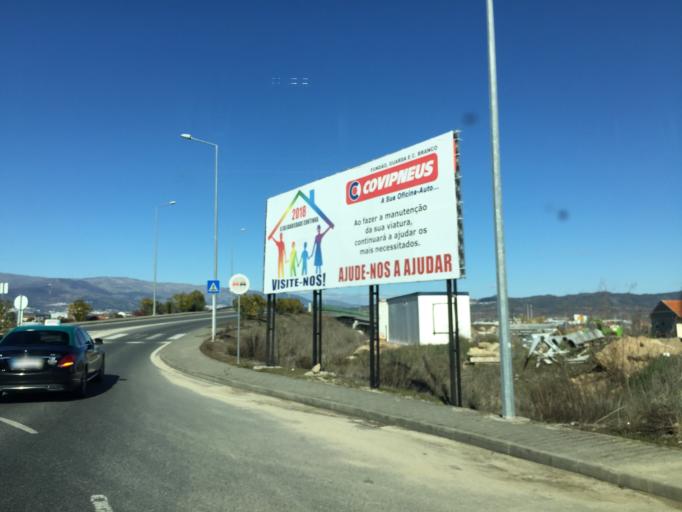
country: PT
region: Castelo Branco
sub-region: Concelho do Fundao
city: Fundao
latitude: 40.1597
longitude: -7.4978
